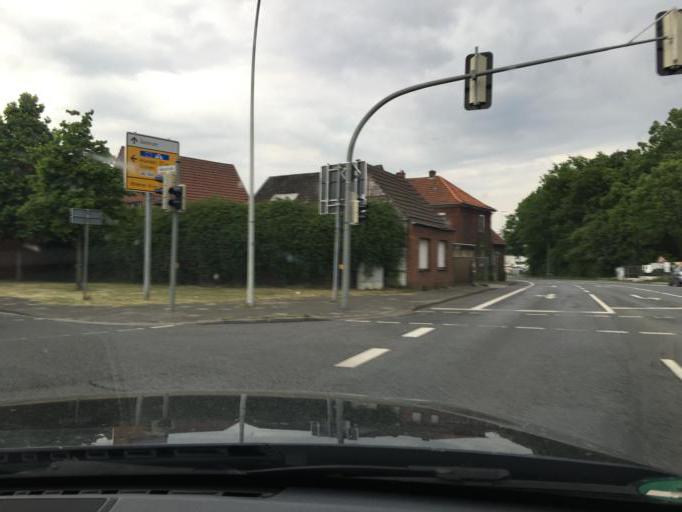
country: DE
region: North Rhine-Westphalia
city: Emsdetten
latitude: 52.1731
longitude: 7.5381
